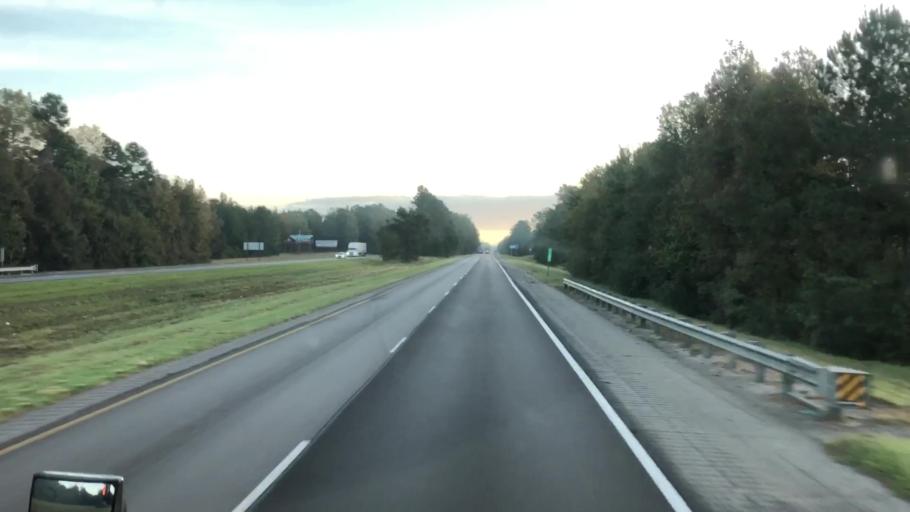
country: US
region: South Carolina
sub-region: Clarendon County
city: Manning
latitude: 33.5794
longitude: -80.3711
